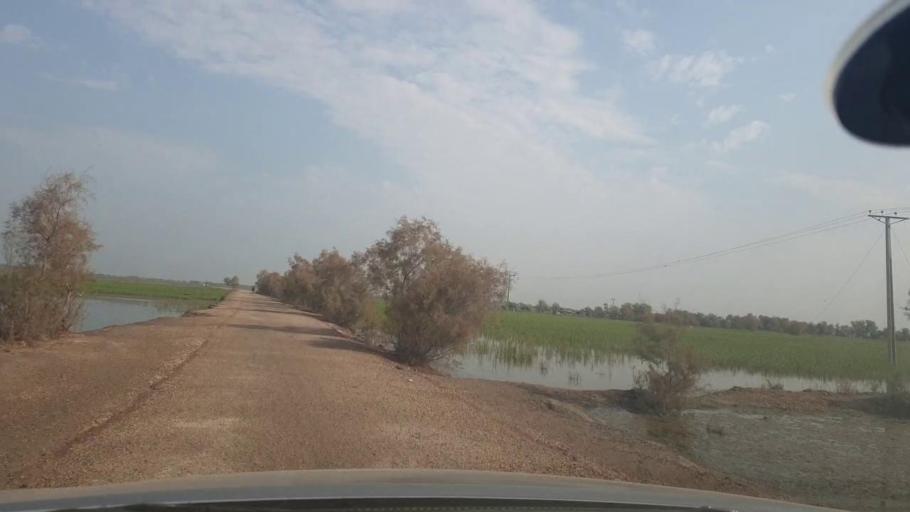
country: PK
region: Balochistan
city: Mehrabpur
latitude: 28.0595
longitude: 68.2108
